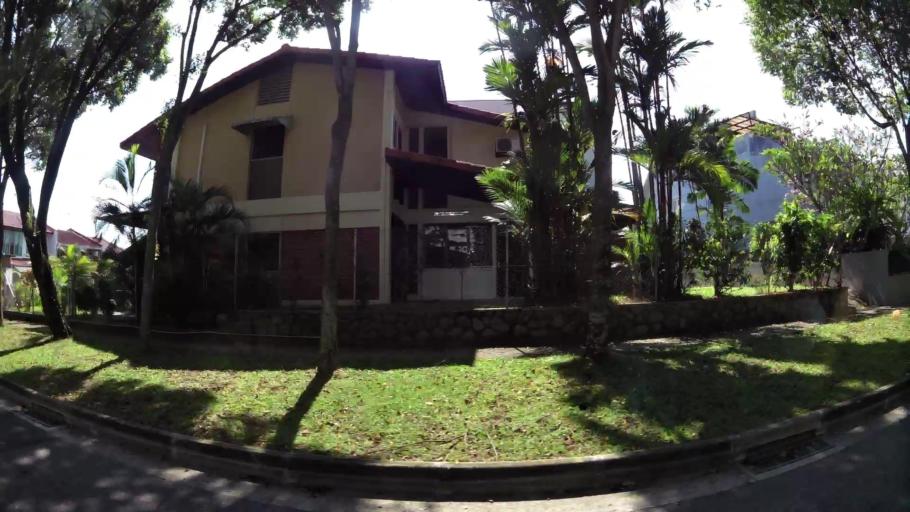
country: SG
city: Singapore
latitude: 1.3768
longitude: 103.8321
